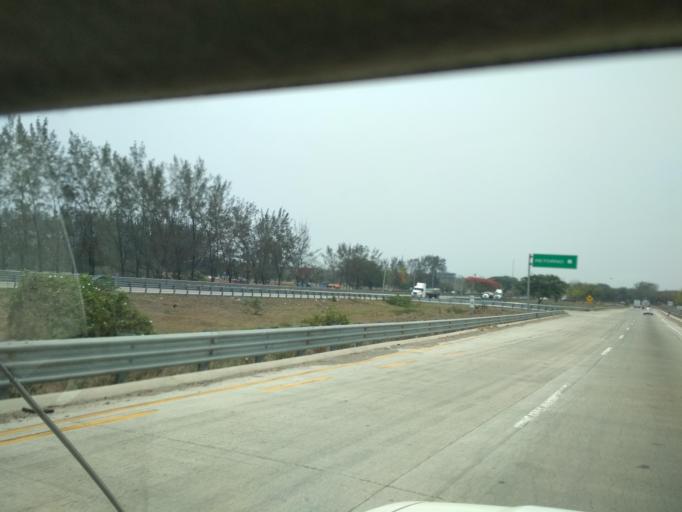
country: MX
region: Veracruz
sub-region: Veracruz
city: Oasis
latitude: 19.1819
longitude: -96.2479
